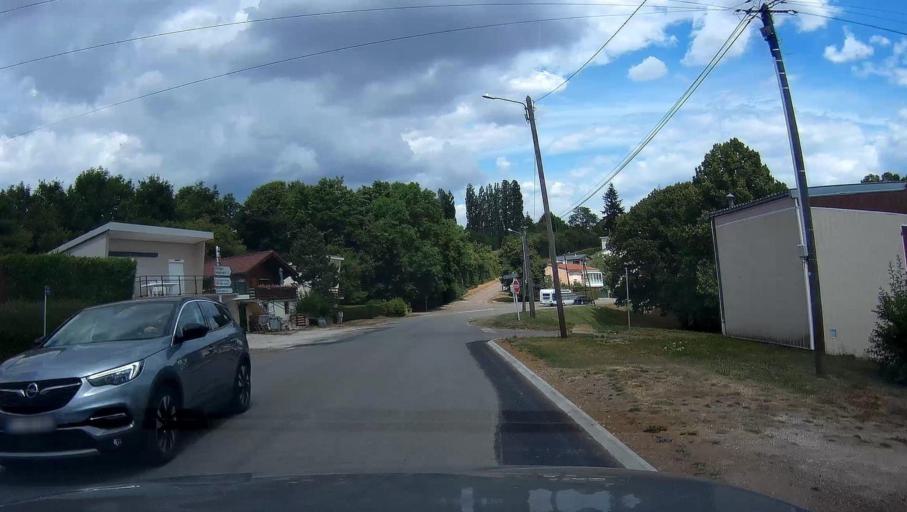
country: FR
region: Champagne-Ardenne
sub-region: Departement de la Haute-Marne
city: Langres
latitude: 47.8693
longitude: 5.3729
